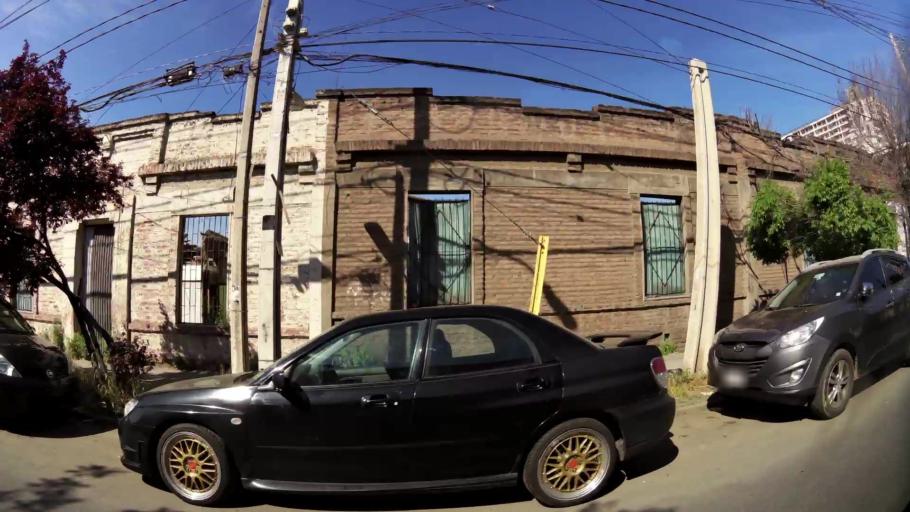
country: CL
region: Santiago Metropolitan
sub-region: Provincia de Santiago
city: Santiago
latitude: -33.4191
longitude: -70.6606
